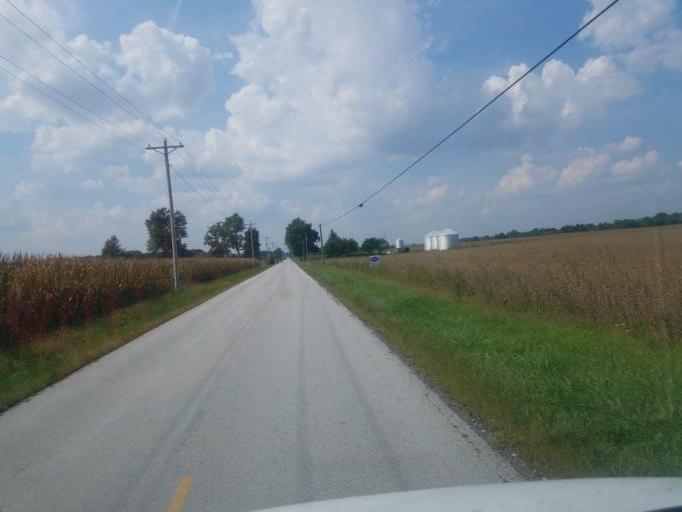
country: US
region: Ohio
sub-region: Hardin County
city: Kenton
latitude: 40.6414
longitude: -83.7455
